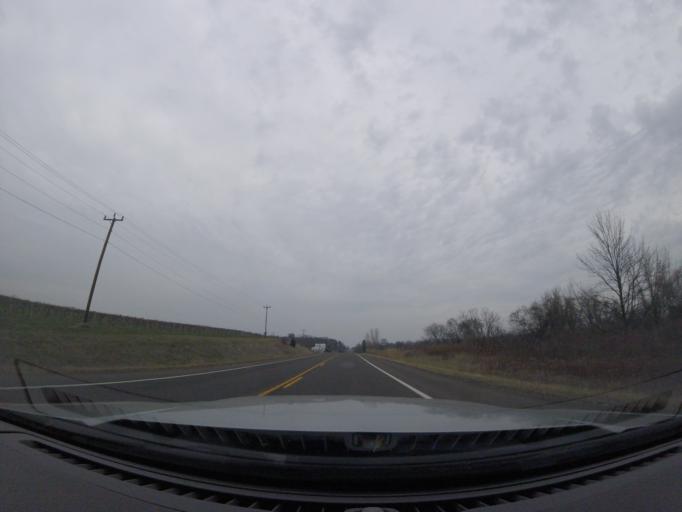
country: US
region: New York
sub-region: Yates County
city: Dundee
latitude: 42.5970
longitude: -76.9439
